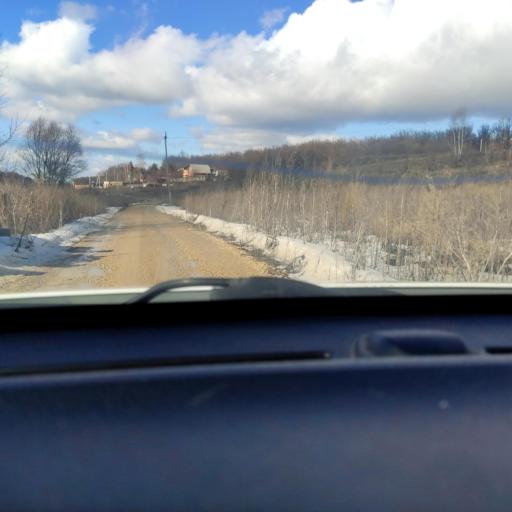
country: RU
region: Voronezj
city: Novaya Usman'
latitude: 51.6831
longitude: 39.3924
